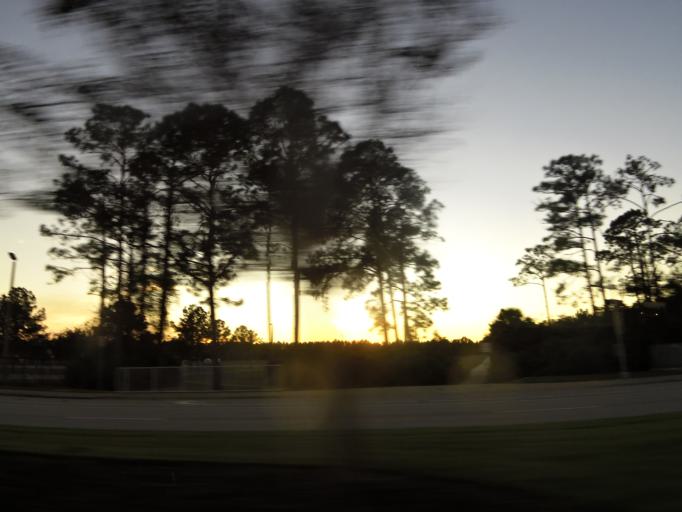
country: US
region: Florida
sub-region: Flagler County
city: Palm Coast
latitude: 29.5806
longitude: -81.2555
